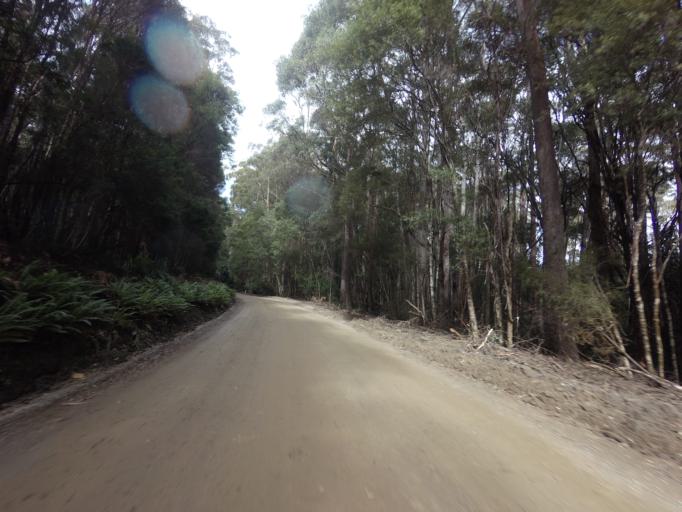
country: AU
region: Tasmania
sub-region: Huon Valley
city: Geeveston
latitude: -43.3990
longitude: 146.8607
